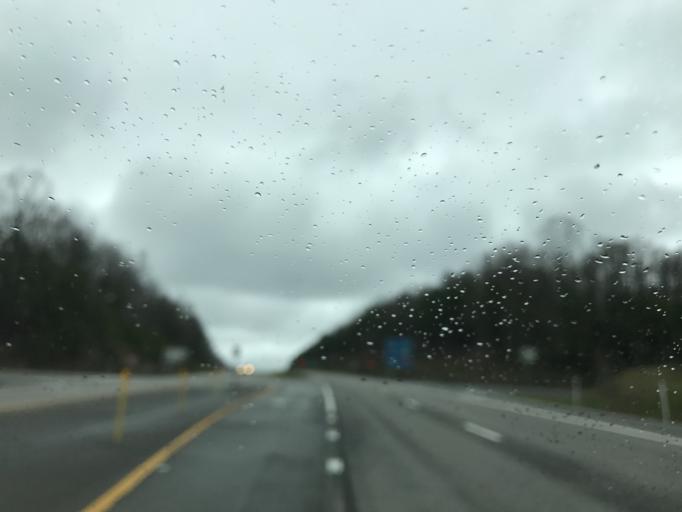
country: US
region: West Virginia
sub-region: Fayette County
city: Fayetteville
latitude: 38.0729
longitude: -81.0751
